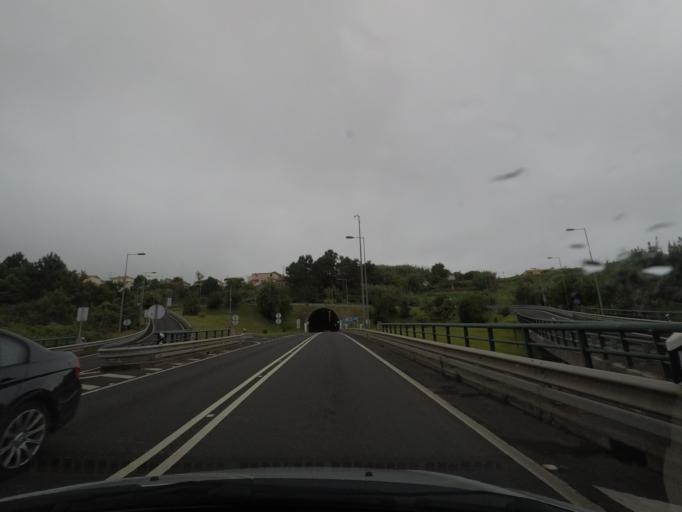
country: PT
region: Madeira
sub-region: Santana
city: Santana
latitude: 32.8099
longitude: -16.8744
